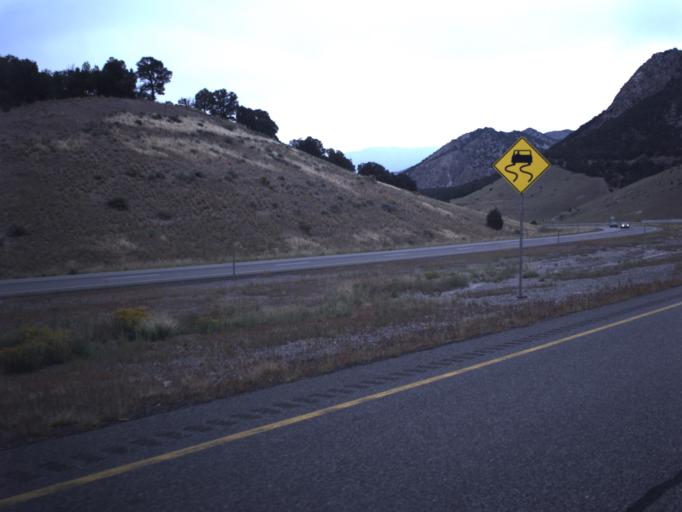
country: US
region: Utah
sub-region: Sevier County
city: Monroe
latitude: 38.5472
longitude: -112.3784
